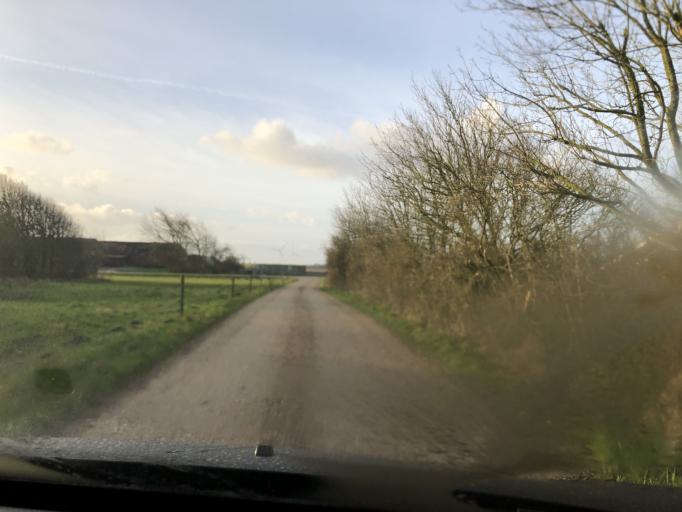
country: DK
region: Central Jutland
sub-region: Ringkobing-Skjern Kommune
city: Skjern
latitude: 55.8746
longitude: 8.3462
